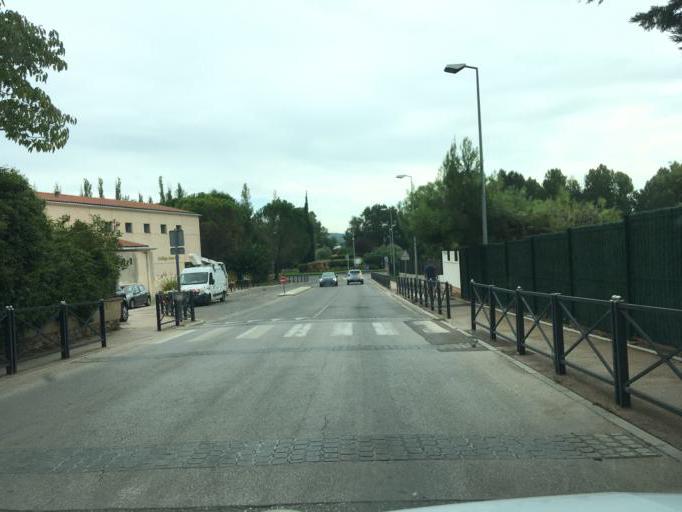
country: FR
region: Provence-Alpes-Cote d'Azur
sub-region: Departement des Bouches-du-Rhone
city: Rousset
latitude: 43.4794
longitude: 5.6244
